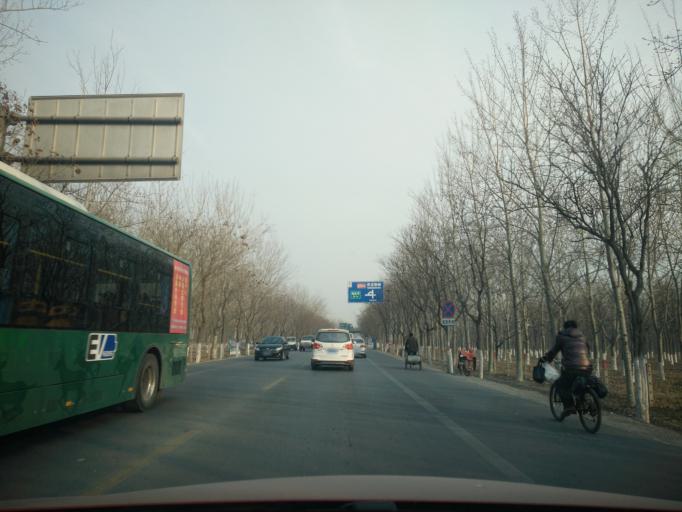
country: CN
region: Beijing
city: Yinghai
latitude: 39.7652
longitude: 116.4073
